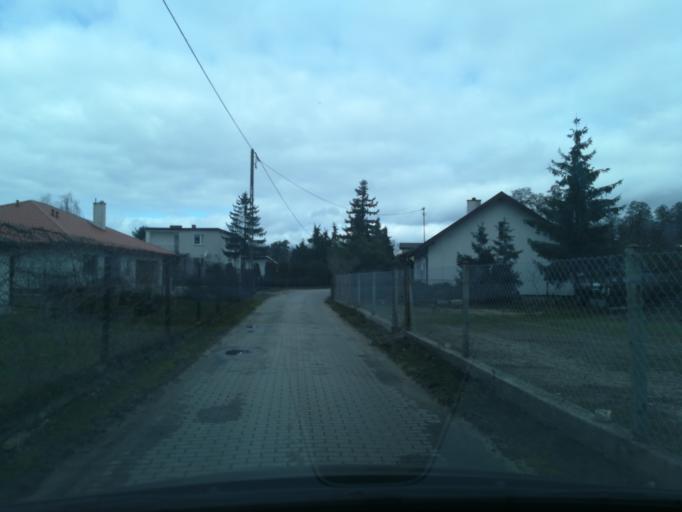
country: PL
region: Kujawsko-Pomorskie
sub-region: Powiat aleksandrowski
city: Ciechocinek
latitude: 52.8751
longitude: 18.7576
